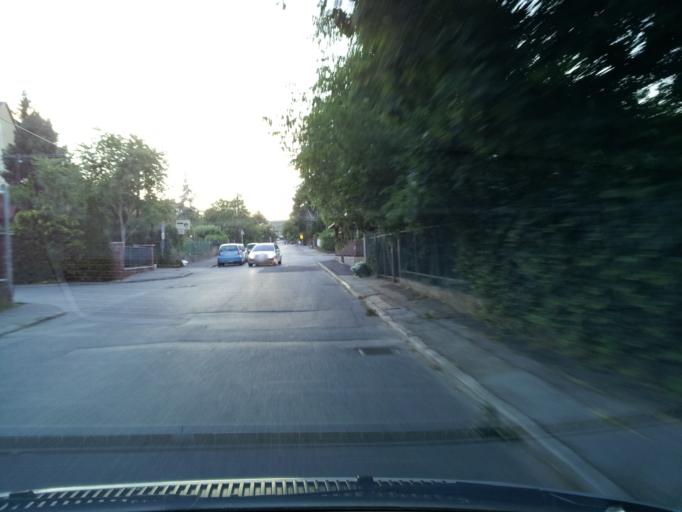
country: HU
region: Veszprem
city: Balatonalmadi
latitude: 47.0305
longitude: 18.0202
